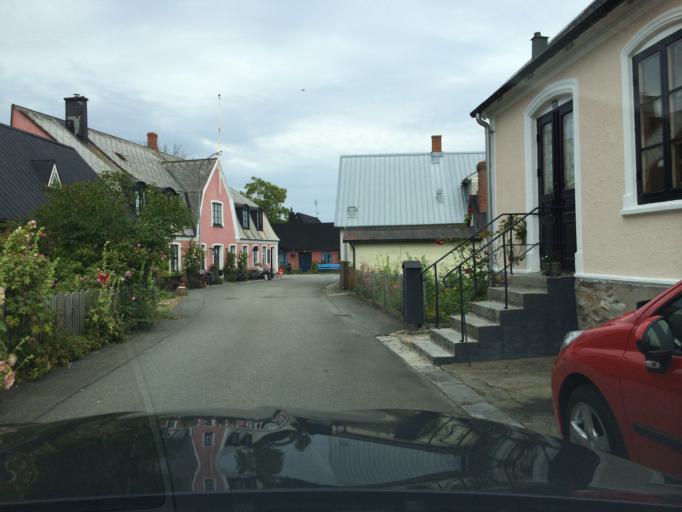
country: SE
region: Skane
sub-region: Simrishamns Kommun
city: Simrishamn
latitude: 55.5141
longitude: 14.3469
